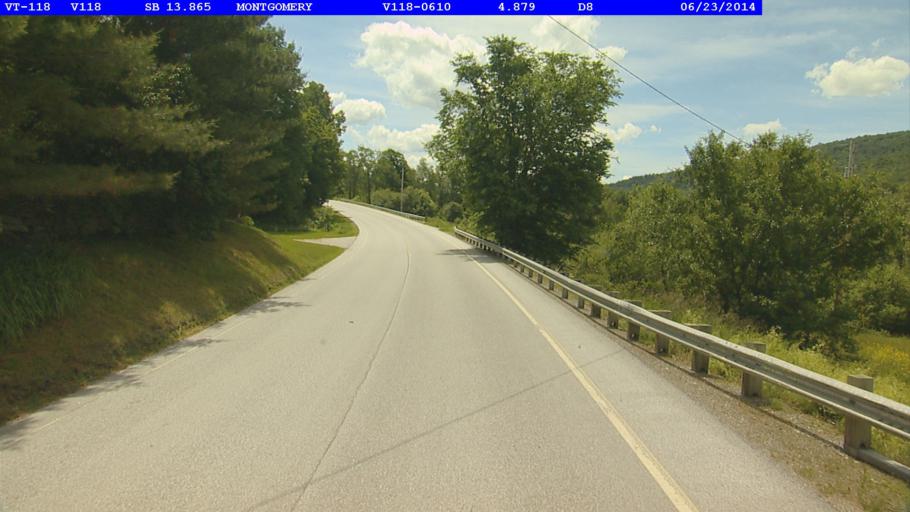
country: US
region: Vermont
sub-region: Franklin County
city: Richford
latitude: 44.8676
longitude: -72.6106
